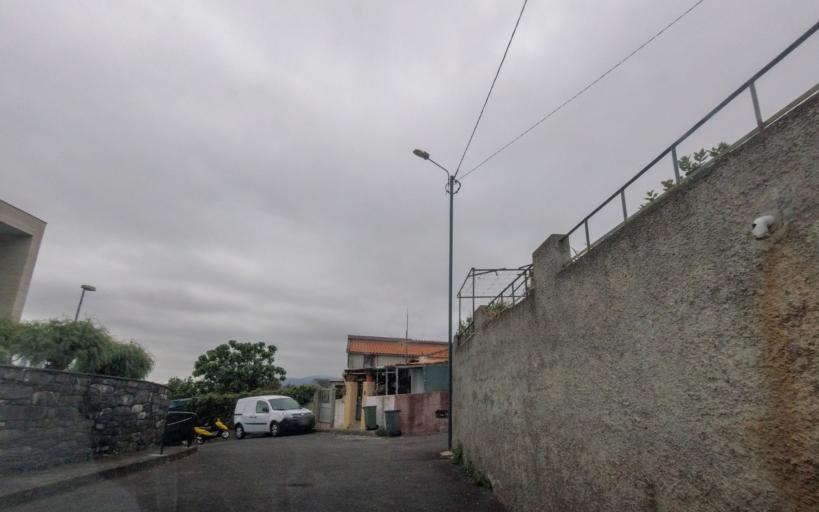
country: PT
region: Madeira
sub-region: Funchal
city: Nossa Senhora do Monte
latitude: 32.6715
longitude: -16.9119
